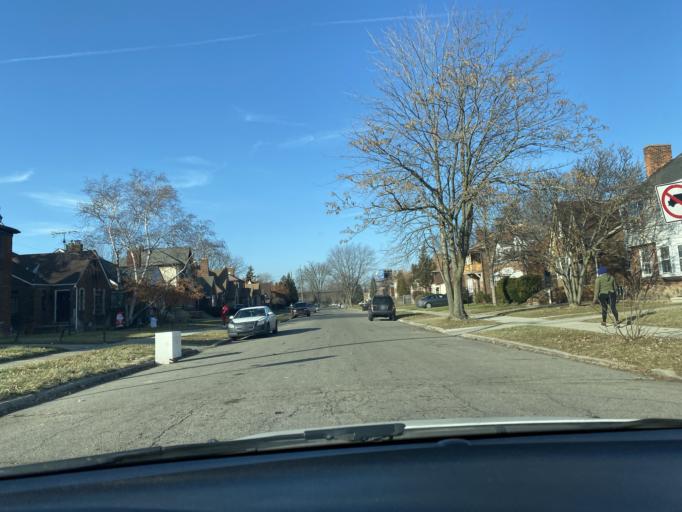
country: US
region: Michigan
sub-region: Wayne County
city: Grosse Pointe Park
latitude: 42.4067
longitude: -82.9452
